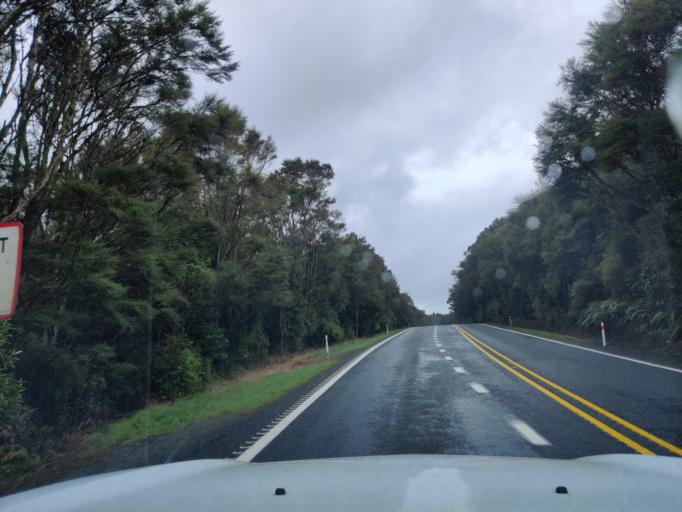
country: NZ
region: Waikato
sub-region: South Waikato District
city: Tokoroa
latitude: -38.0219
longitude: 175.9568
